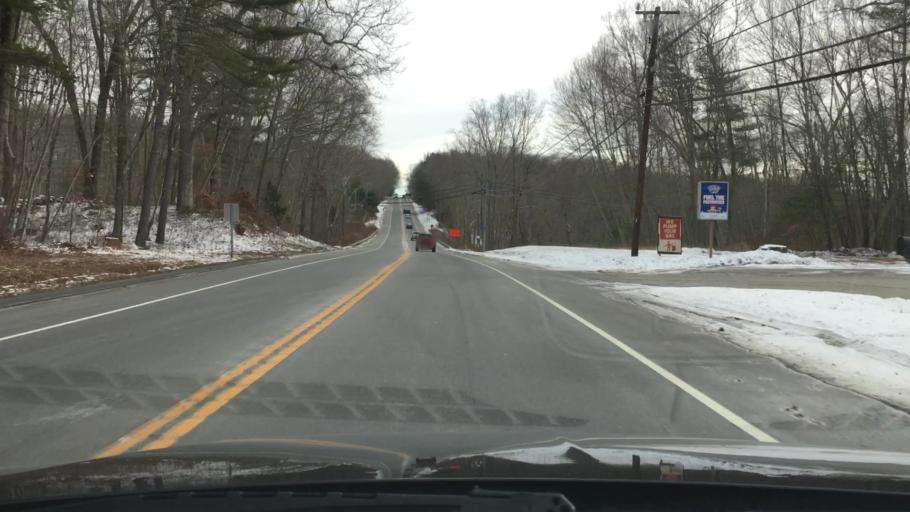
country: US
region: Connecticut
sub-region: New London County
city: Ledyard Center
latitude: 41.4935
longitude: -72.0255
